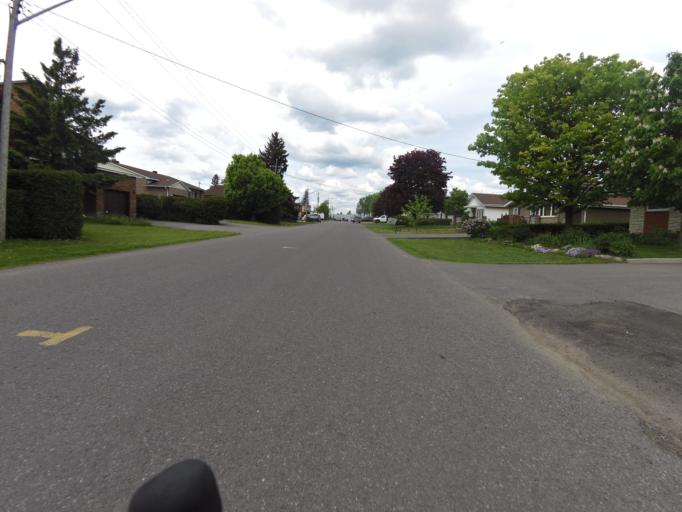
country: CA
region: Ontario
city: Ottawa
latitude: 45.4178
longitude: -75.6260
